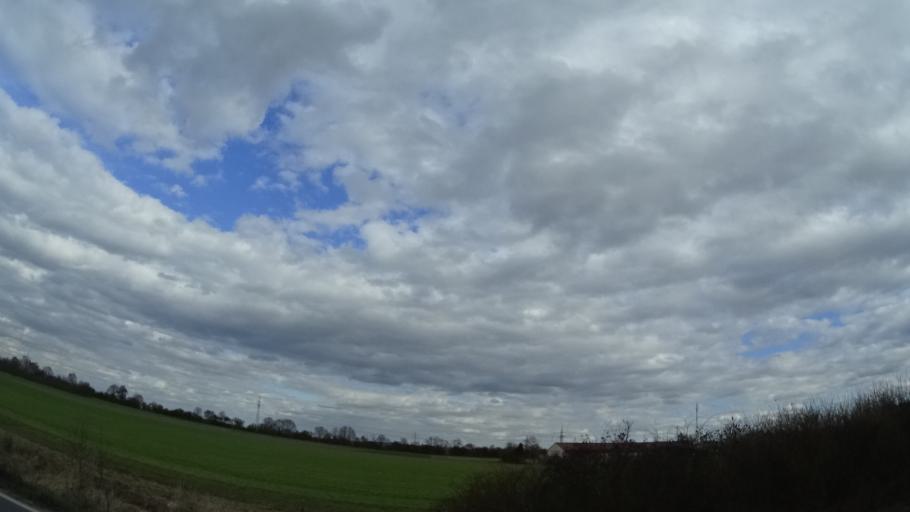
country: DE
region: Hesse
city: Biebesheim
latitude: 49.7839
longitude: 8.4896
